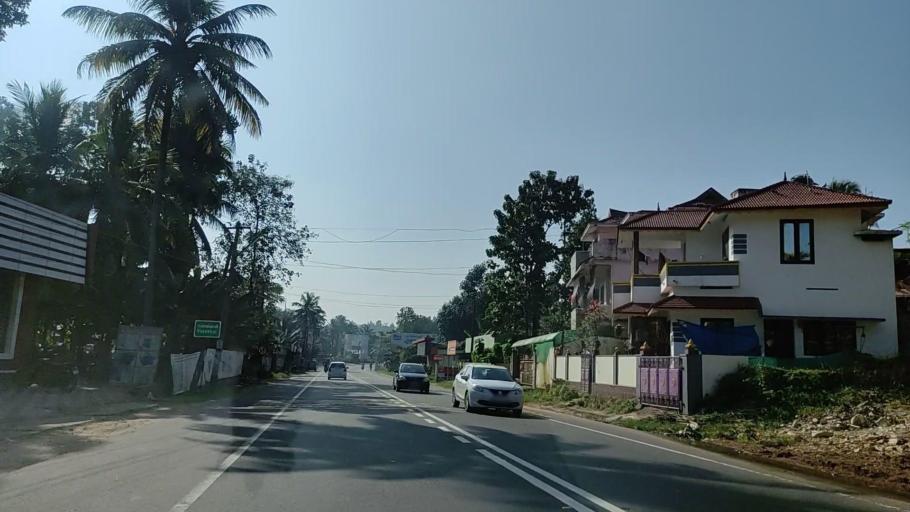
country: IN
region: Kerala
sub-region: Kollam
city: Punalur
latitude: 8.9279
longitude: 76.8543
